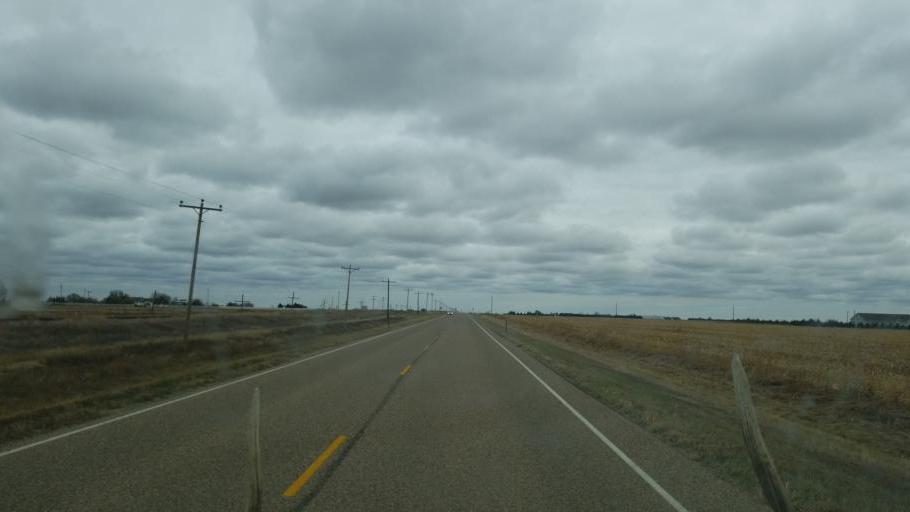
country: US
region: Colorado
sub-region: Kiowa County
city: Eads
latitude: 38.4849
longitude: -102.8451
